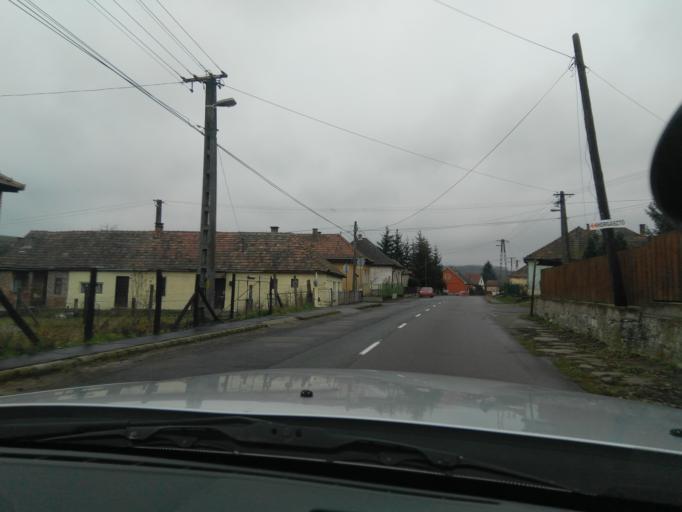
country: HU
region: Nograd
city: Matraterenye
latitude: 48.0333
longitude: 19.9470
